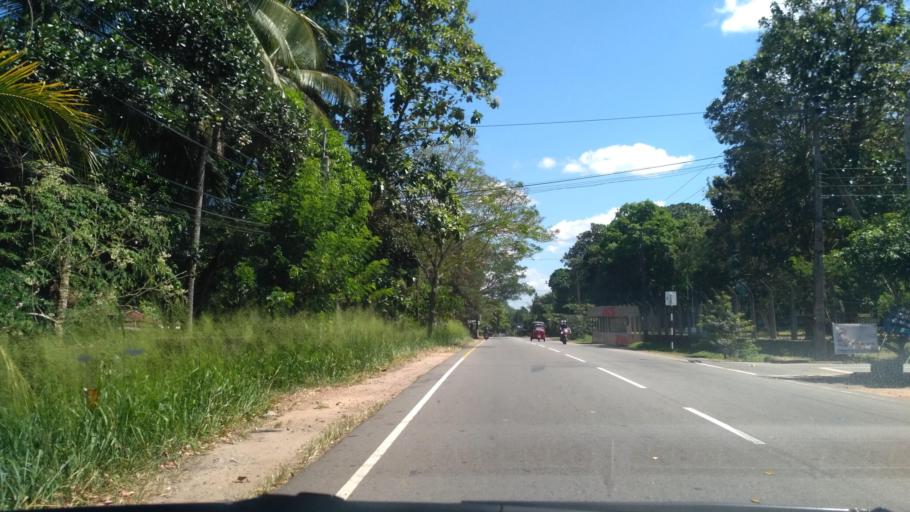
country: LK
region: North Western
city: Kuliyapitiya
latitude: 7.3228
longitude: 80.0910
